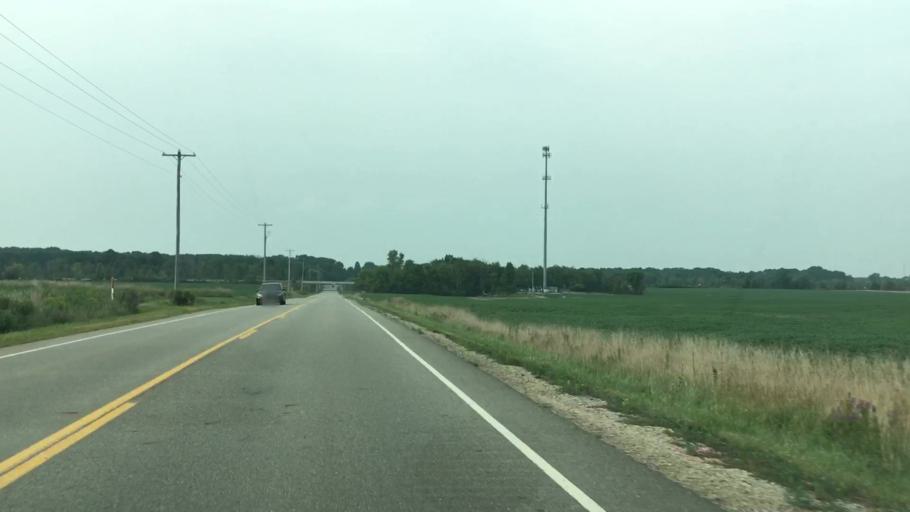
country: US
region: Michigan
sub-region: Ottawa County
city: Hudsonville
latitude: 42.8300
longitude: -85.9006
